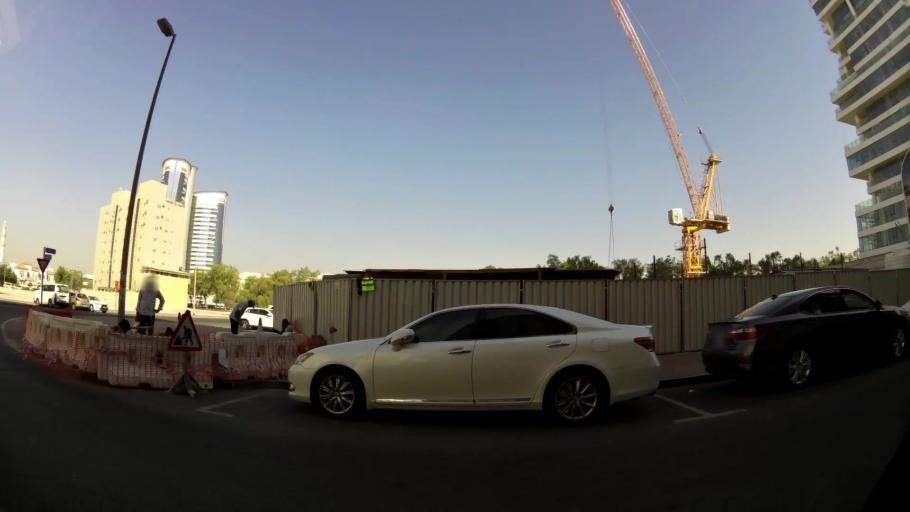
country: AE
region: Ash Shariqah
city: Sharjah
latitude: 25.2519
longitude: 55.2923
